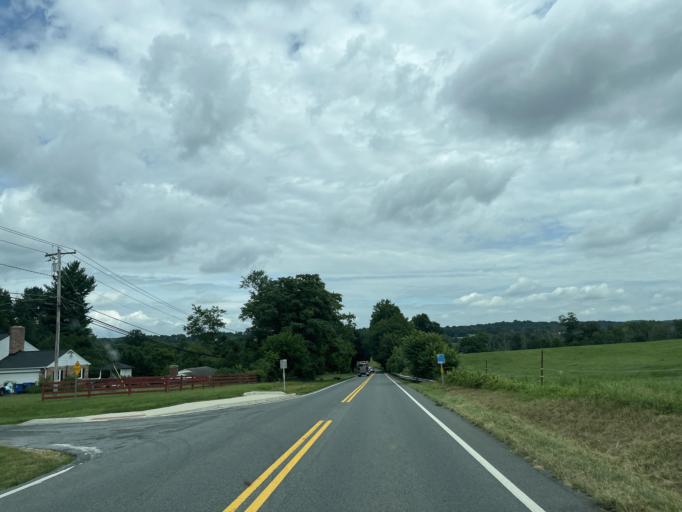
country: US
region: Maryland
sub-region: Montgomery County
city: Montgomery Village
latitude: 39.2302
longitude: -77.1782
